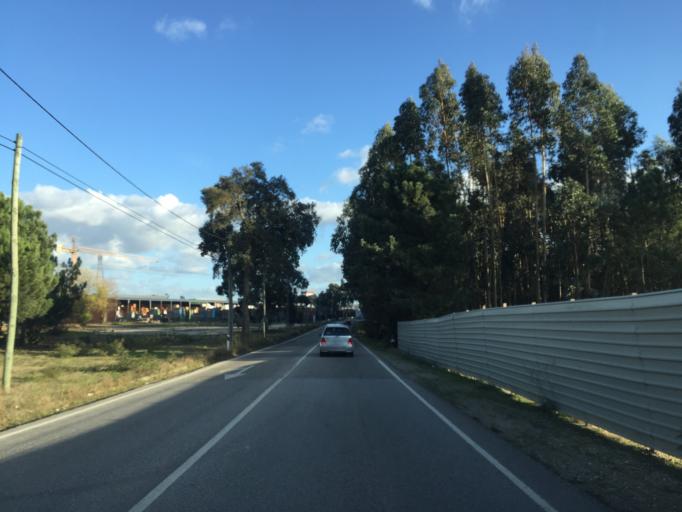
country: PT
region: Leiria
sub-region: Leiria
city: Amor
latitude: 39.7943
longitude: -8.8340
